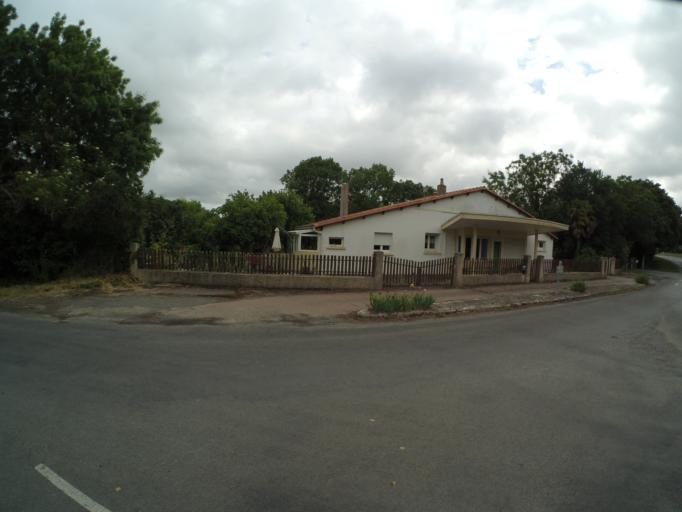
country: FR
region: Poitou-Charentes
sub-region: Departement de la Charente-Maritime
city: Saint-Laurent-de-la-Pree
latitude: 45.9937
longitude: -1.0335
